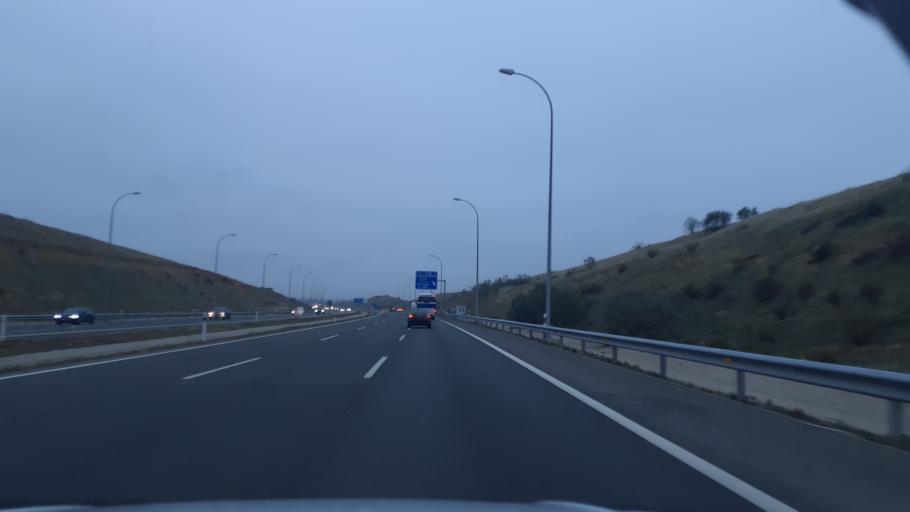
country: ES
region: Madrid
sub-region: Provincia de Madrid
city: Paracuellos de Jarama
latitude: 40.4920
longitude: -3.4962
